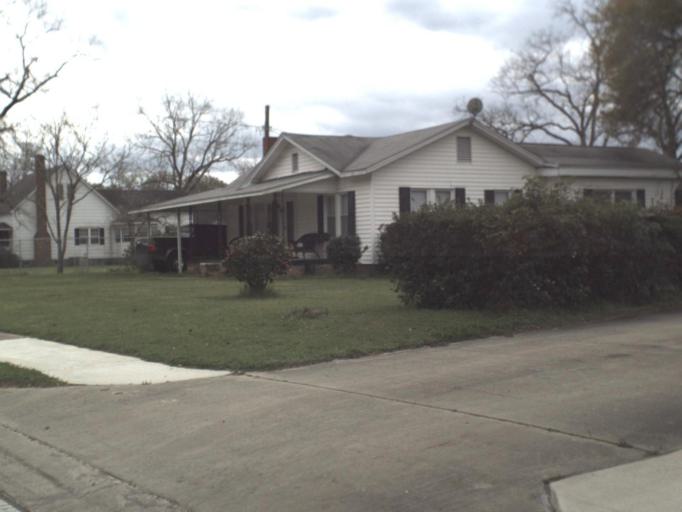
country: US
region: Florida
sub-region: Gadsden County
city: Quincy
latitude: 30.5655
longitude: -84.5930
